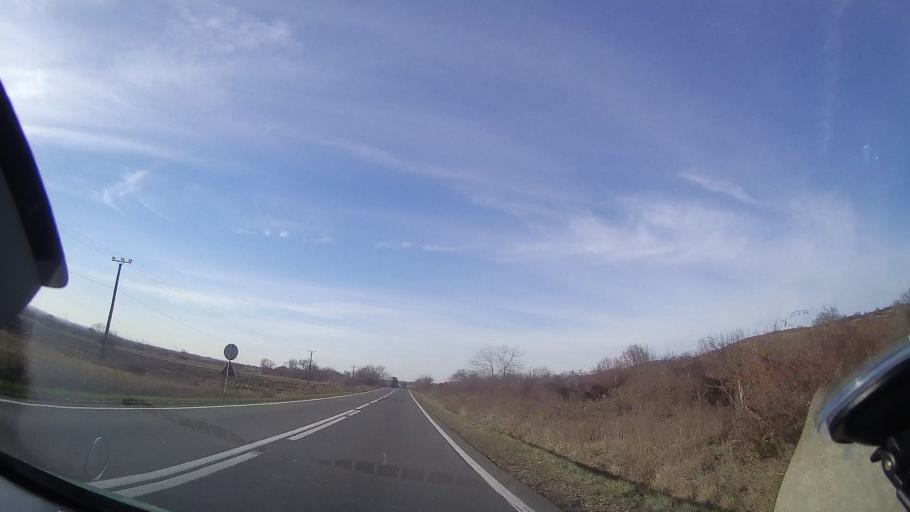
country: RO
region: Bihor
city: Lugasu de Jos
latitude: 47.0655
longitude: 22.3095
